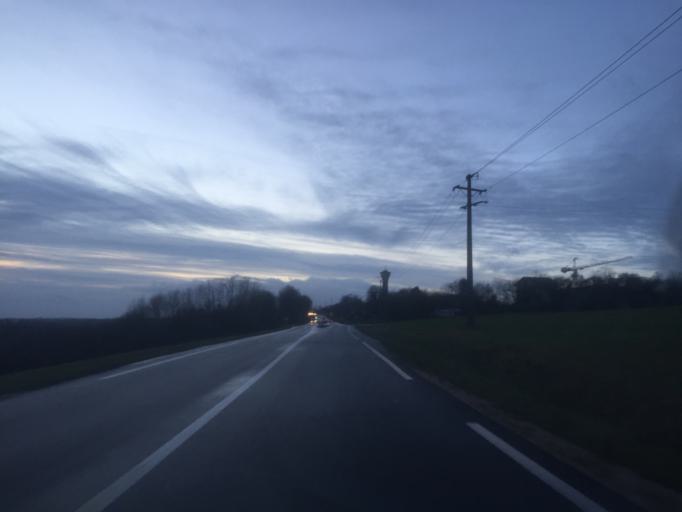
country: FR
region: Franche-Comte
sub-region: Departement du Jura
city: Orchamps
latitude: 47.1465
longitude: 5.6322
